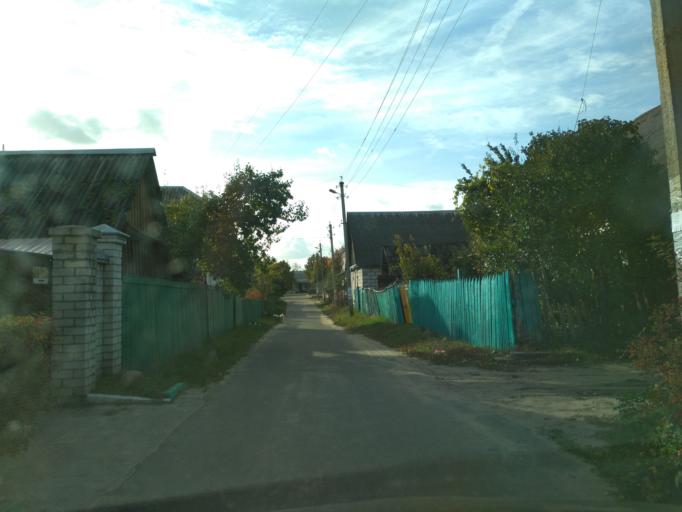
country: BY
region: Minsk
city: Mar''ina Horka
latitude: 53.5076
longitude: 28.1516
